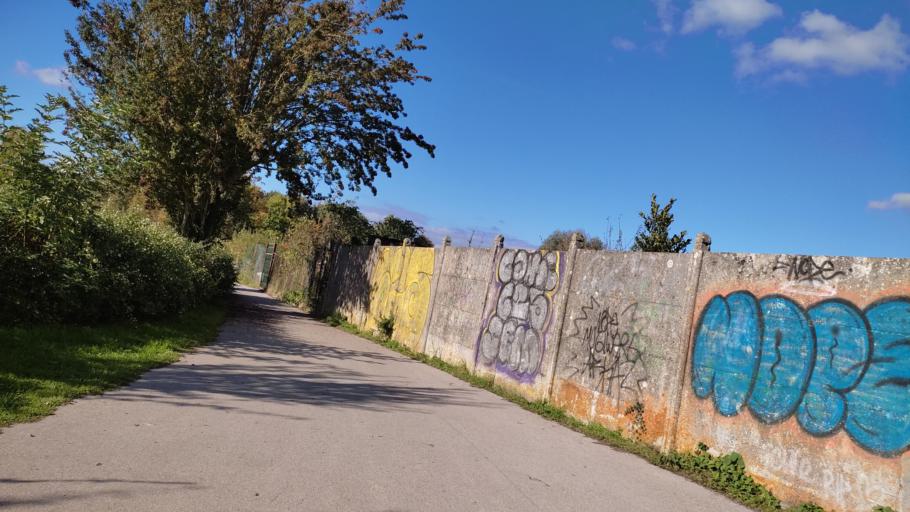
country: FR
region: Nord-Pas-de-Calais
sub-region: Departement du Pas-de-Calais
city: Saint-Nicolas
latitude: 50.3028
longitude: 2.7721
